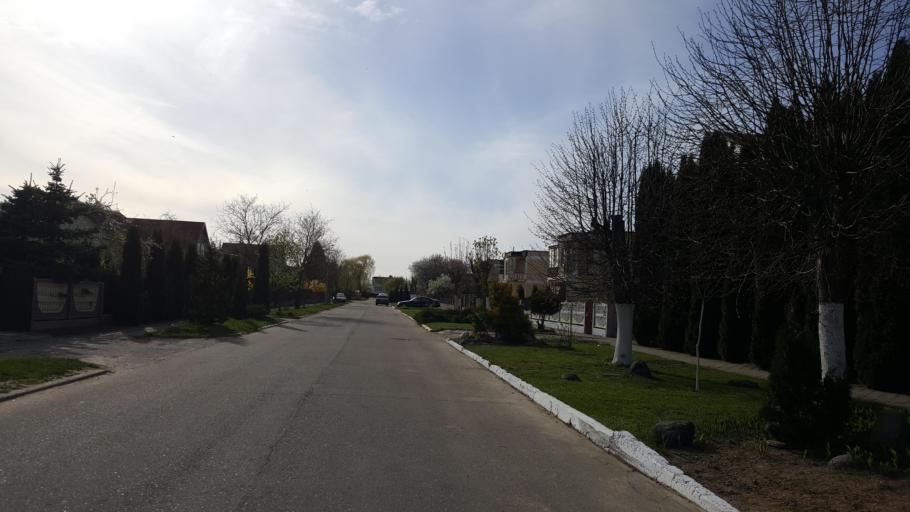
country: BY
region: Brest
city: Vysokaye
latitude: 52.4011
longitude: 23.4590
